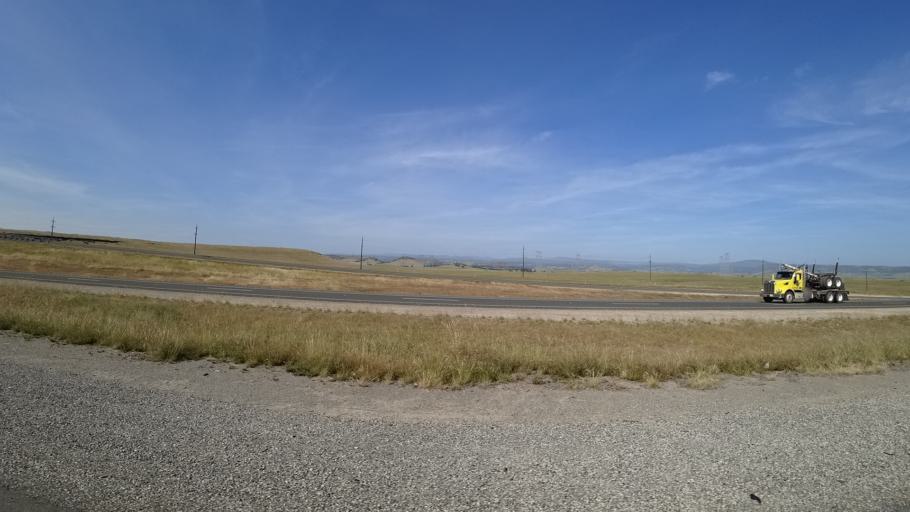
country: US
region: California
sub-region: Butte County
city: Durham
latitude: 39.6199
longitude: -121.6903
